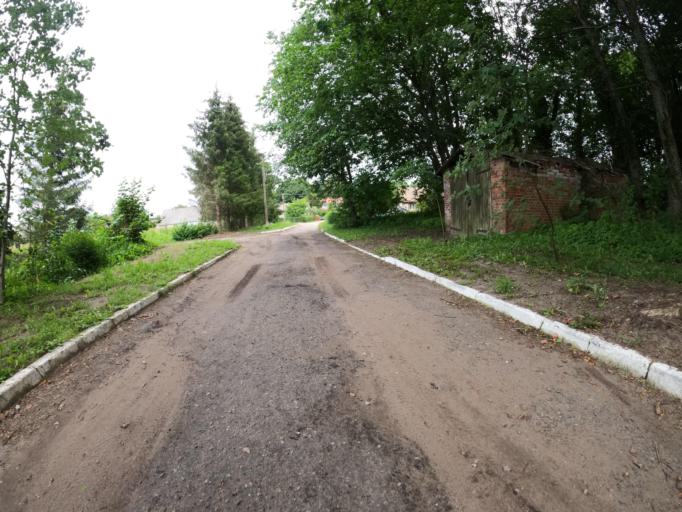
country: PL
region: West Pomeranian Voivodeship
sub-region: Powiat bialogardzki
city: Tychowo
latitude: 54.0017
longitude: 16.3740
